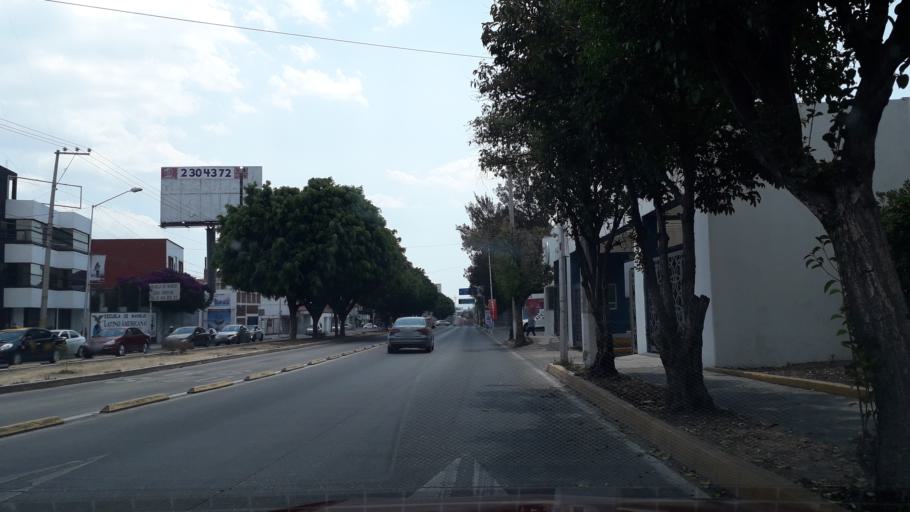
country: MX
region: Puebla
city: Puebla
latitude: 19.0300
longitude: -98.2180
